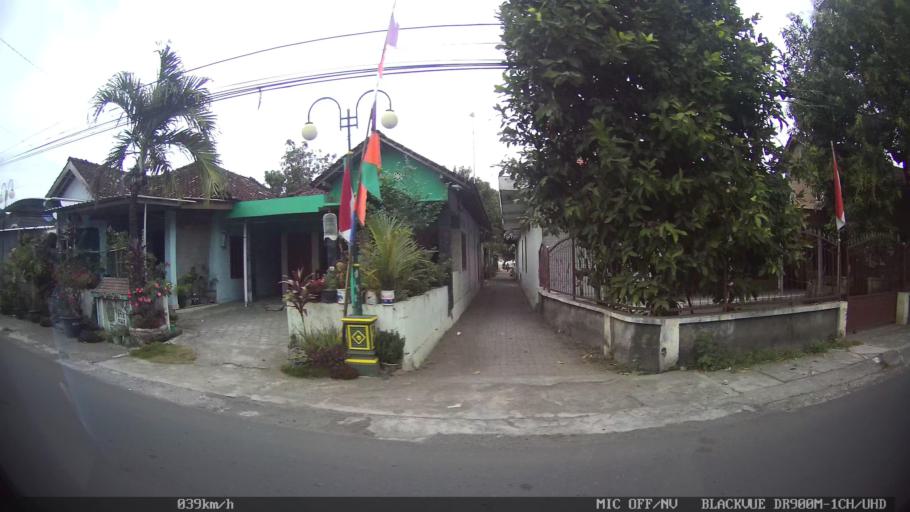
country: ID
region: Daerah Istimewa Yogyakarta
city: Sewon
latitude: -7.8786
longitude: 110.4133
